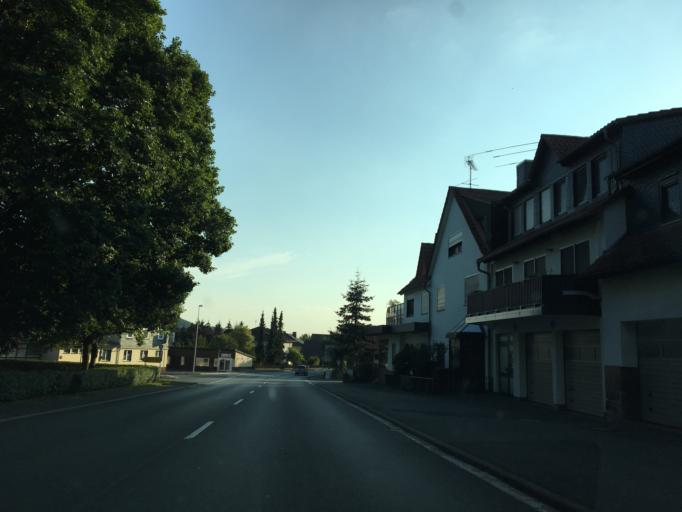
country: DE
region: Hesse
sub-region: Regierungsbezirk Giessen
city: Munchhausen
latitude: 50.9858
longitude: 8.7389
